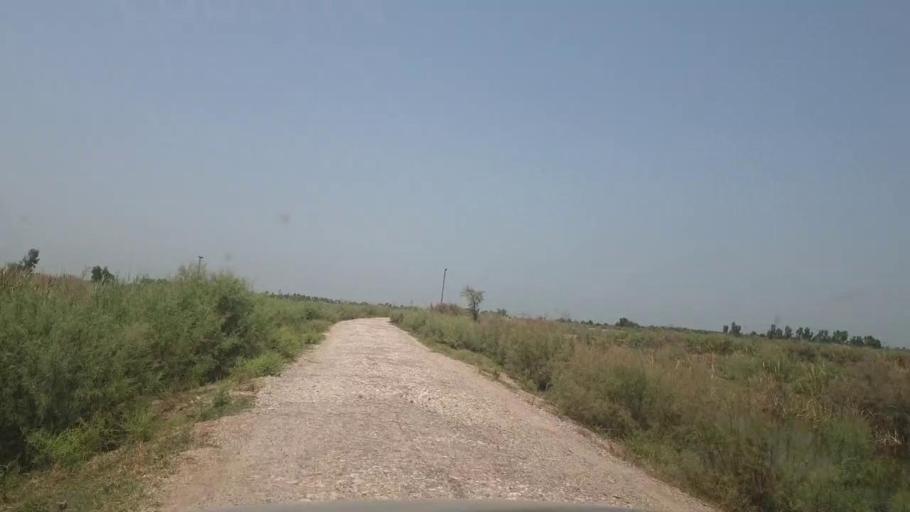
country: PK
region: Sindh
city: Lakhi
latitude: 27.8466
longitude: 68.6250
